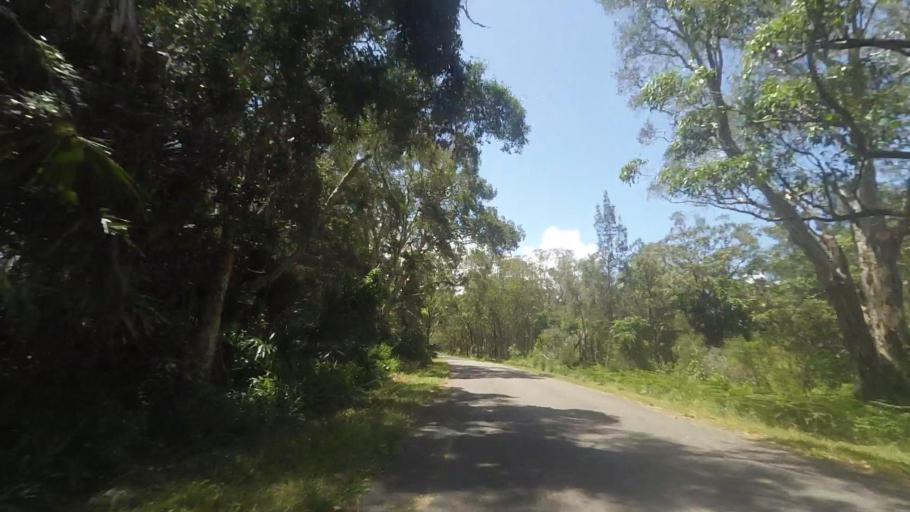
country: AU
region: New South Wales
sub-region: Great Lakes
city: Bulahdelah
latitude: -32.5298
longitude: 152.3228
